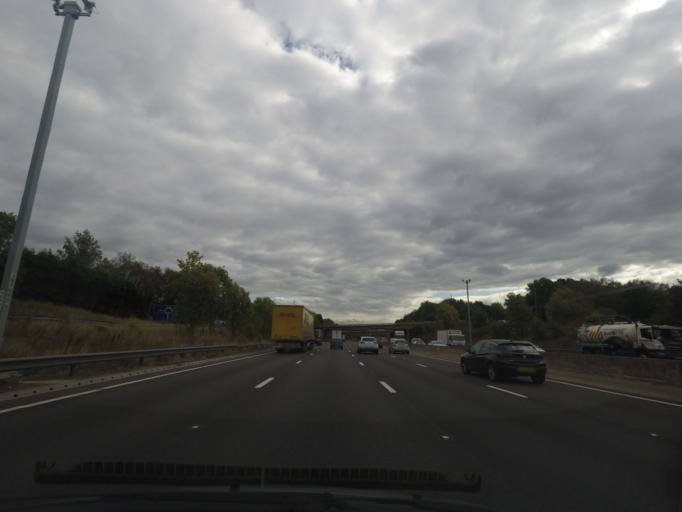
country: GB
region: England
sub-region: Sheffield
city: Chapletown
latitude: 53.4579
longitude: -1.4461
